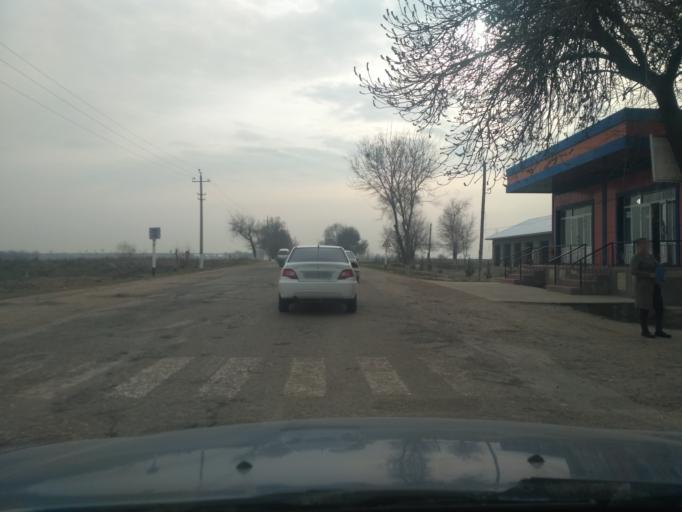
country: UZ
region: Sirdaryo
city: Sirdaryo
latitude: 40.8264
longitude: 68.6057
